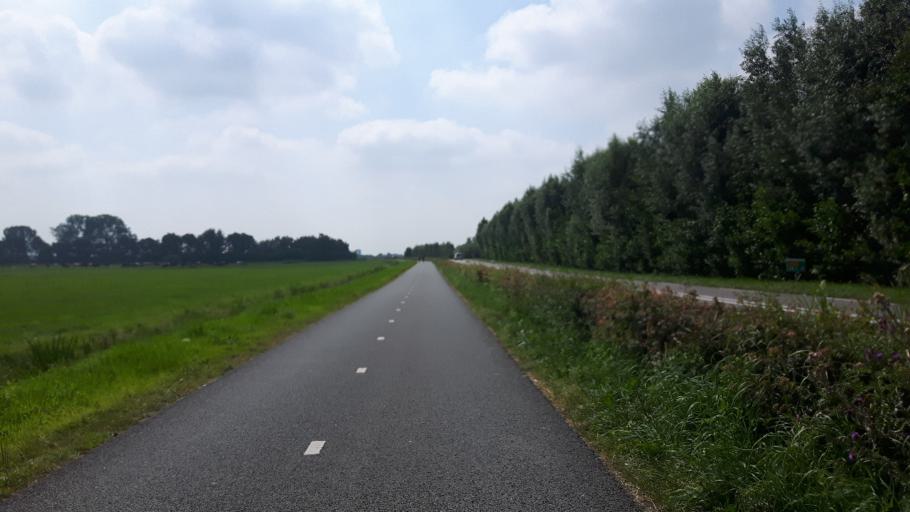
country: NL
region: Utrecht
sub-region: Gemeente Montfoort
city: Montfoort
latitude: 52.0198
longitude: 4.9511
